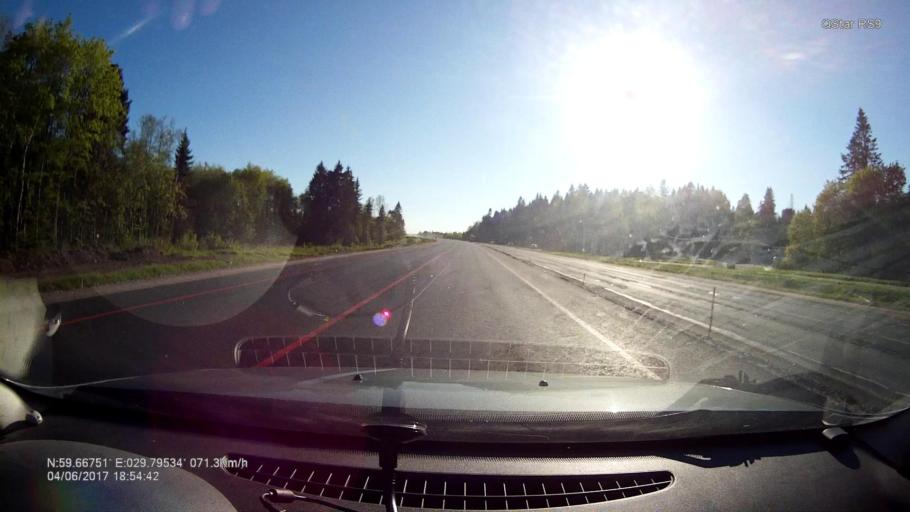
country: RU
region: Leningrad
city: Kipen'
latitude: 59.6675
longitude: 29.7951
